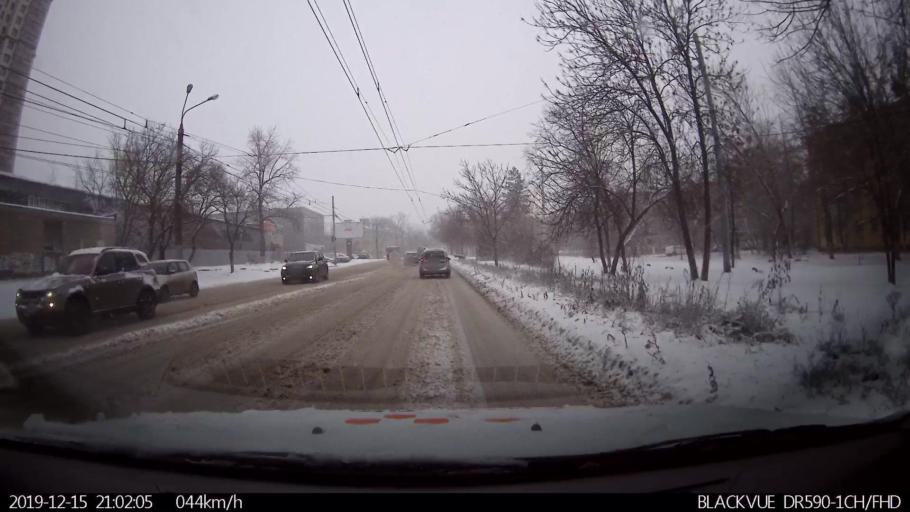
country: RU
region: Nizjnij Novgorod
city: Nizhniy Novgorod
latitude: 56.3080
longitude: 43.9442
